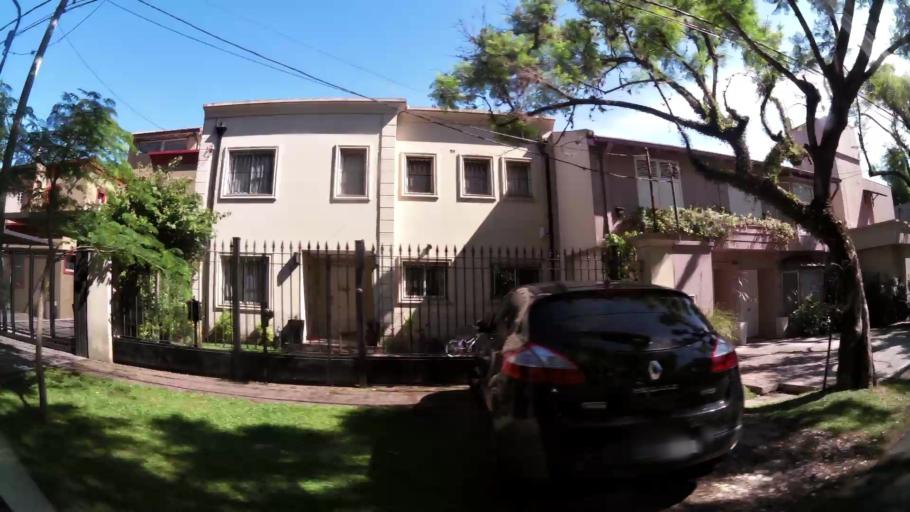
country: AR
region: Buenos Aires
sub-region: Partido de Tigre
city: Tigre
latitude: -34.4825
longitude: -58.5661
